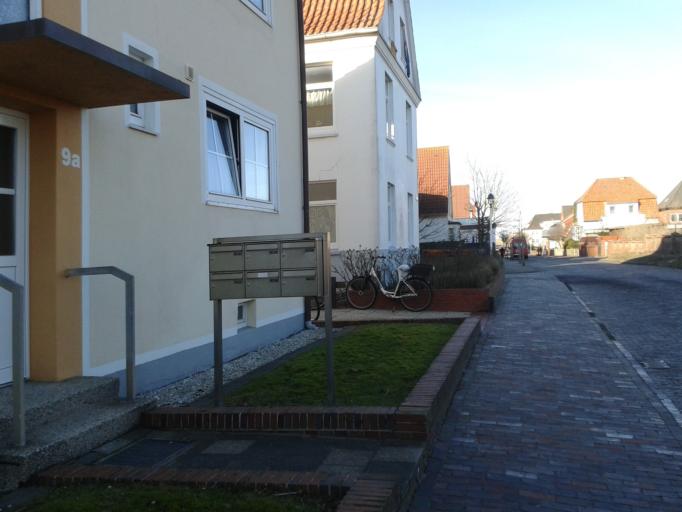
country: DE
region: Lower Saxony
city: Norderney
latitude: 53.7087
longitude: 7.1516
